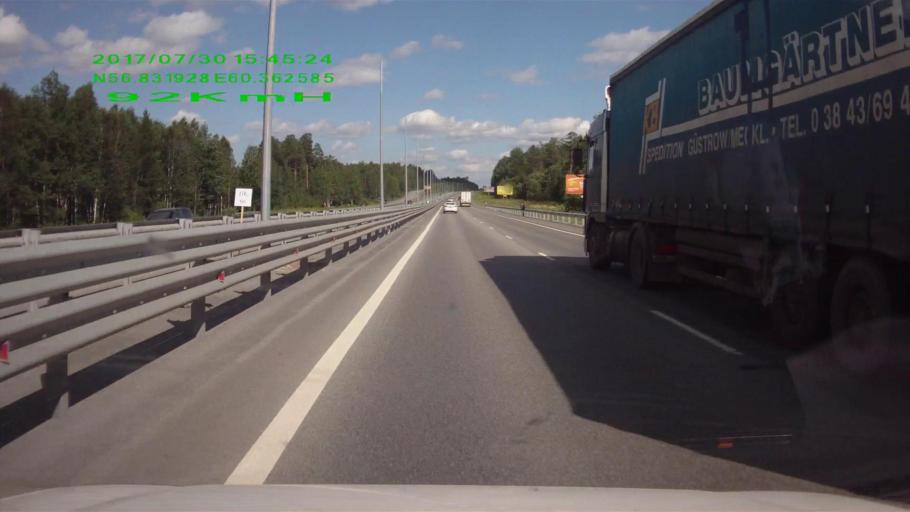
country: RU
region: Sverdlovsk
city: Severka
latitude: 56.8319
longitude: 60.3633
